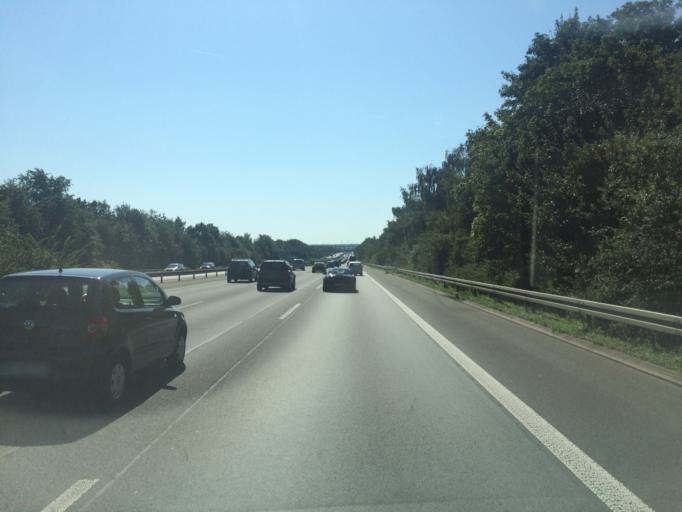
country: DE
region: North Rhine-Westphalia
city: Kamen
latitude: 51.5609
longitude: 7.6646
